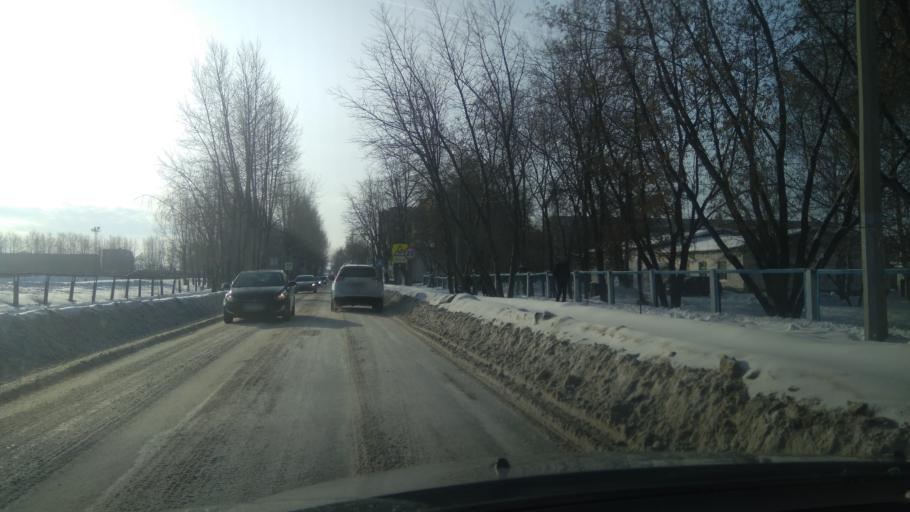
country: RU
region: Sverdlovsk
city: Sukhoy Log
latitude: 56.9024
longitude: 62.0306
